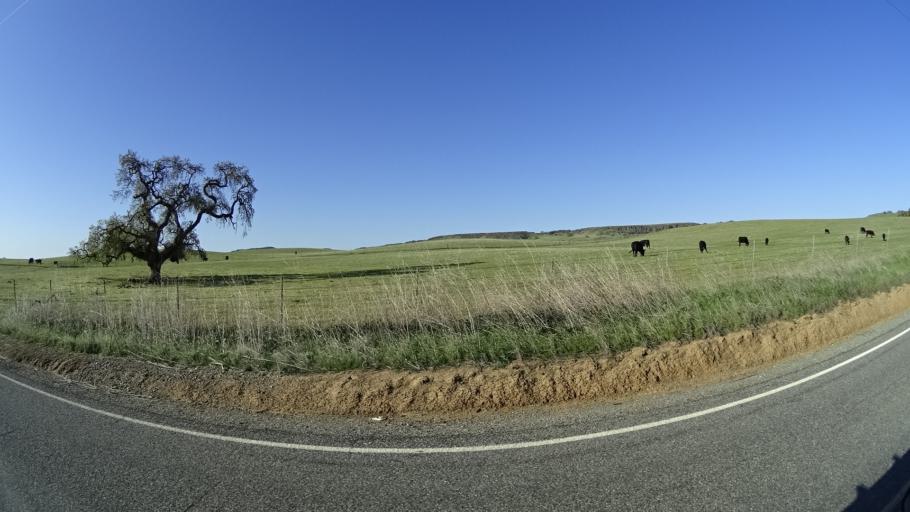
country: US
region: California
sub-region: Glenn County
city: Orland
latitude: 39.7999
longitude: -122.3217
